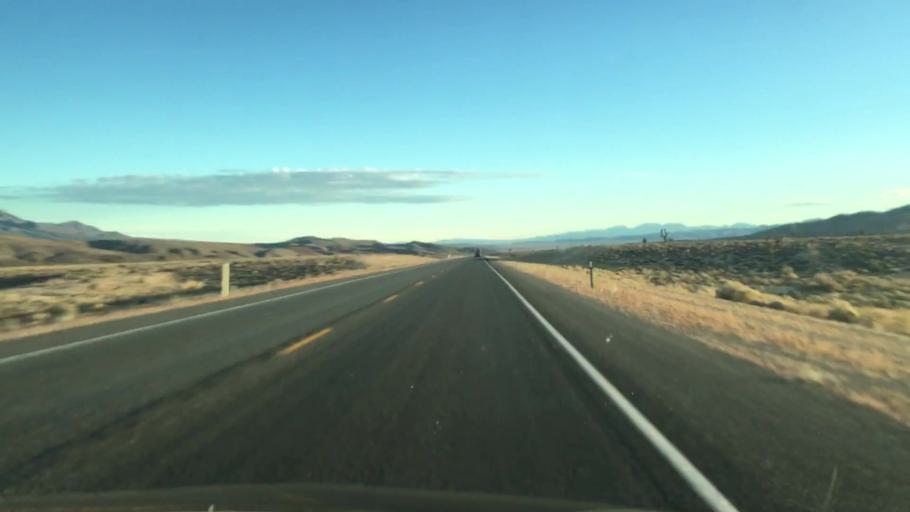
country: US
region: Nevada
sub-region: Esmeralda County
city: Goldfield
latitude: 37.5911
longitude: -117.2089
